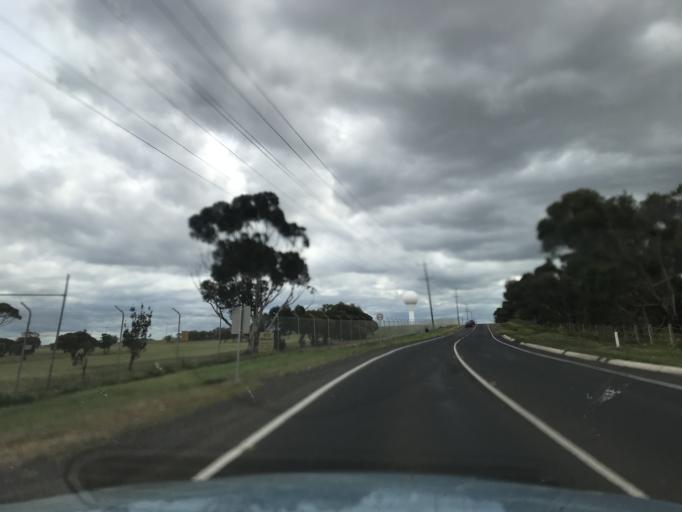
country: AU
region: Victoria
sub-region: Hobsons Bay
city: Laverton
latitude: -37.8552
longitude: 144.7606
